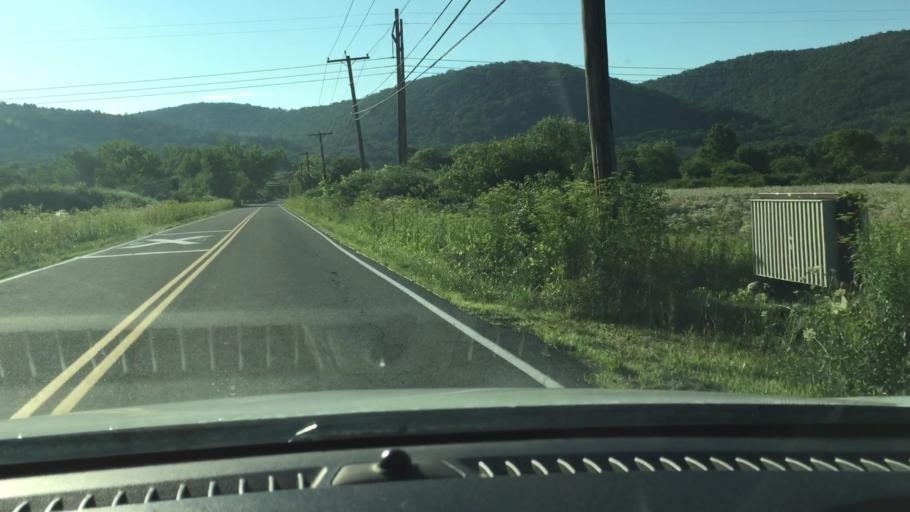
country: US
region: Massachusetts
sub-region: Berkshire County
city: Lenox
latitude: 42.3949
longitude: -73.2456
